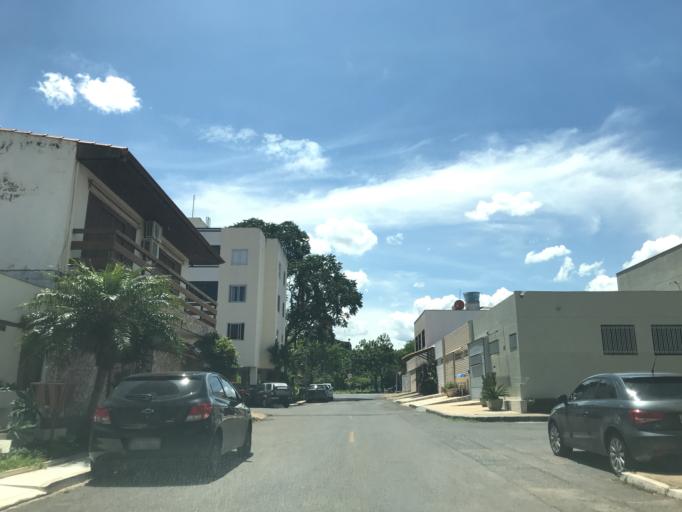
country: BR
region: Federal District
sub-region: Brasilia
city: Brasilia
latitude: -15.7792
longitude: -47.8898
